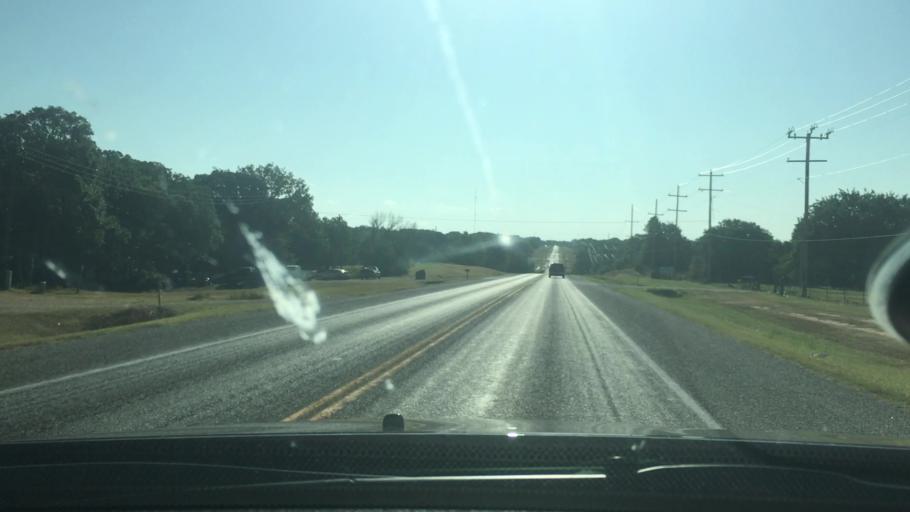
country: US
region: Oklahoma
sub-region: Johnston County
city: Tishomingo
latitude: 34.2368
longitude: -96.7233
